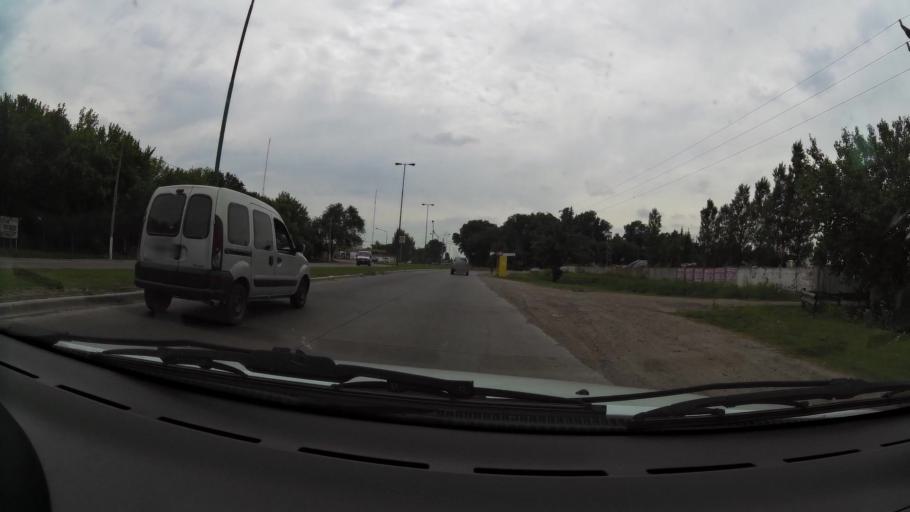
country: AR
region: Buenos Aires
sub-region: Partido de La Plata
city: La Plata
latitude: -34.9138
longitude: -58.0081
